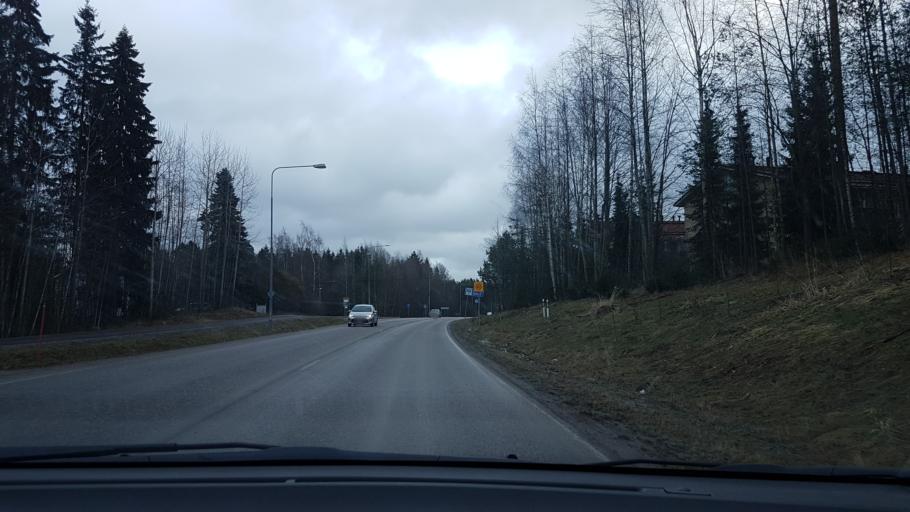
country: FI
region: Uusimaa
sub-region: Helsinki
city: Kerava
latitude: 60.3710
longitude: 25.0683
